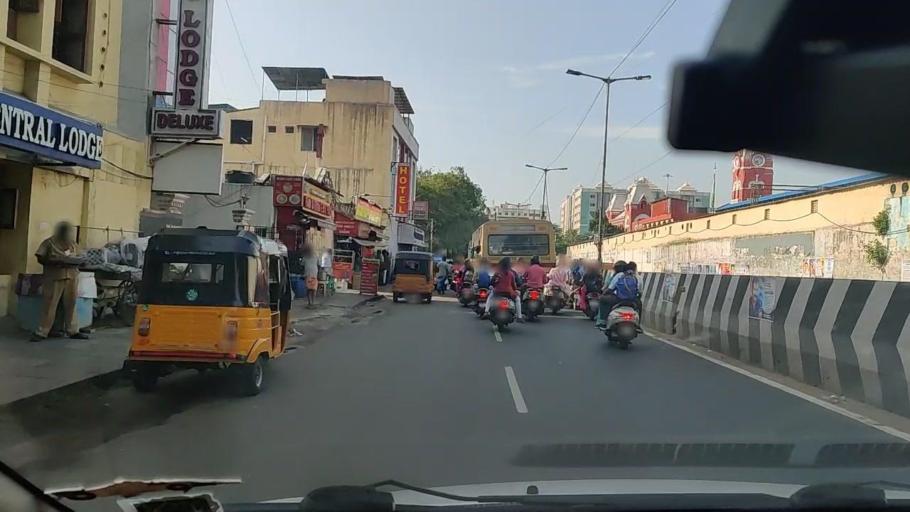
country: IN
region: Tamil Nadu
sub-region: Chennai
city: Chennai
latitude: 13.0841
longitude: 80.2761
